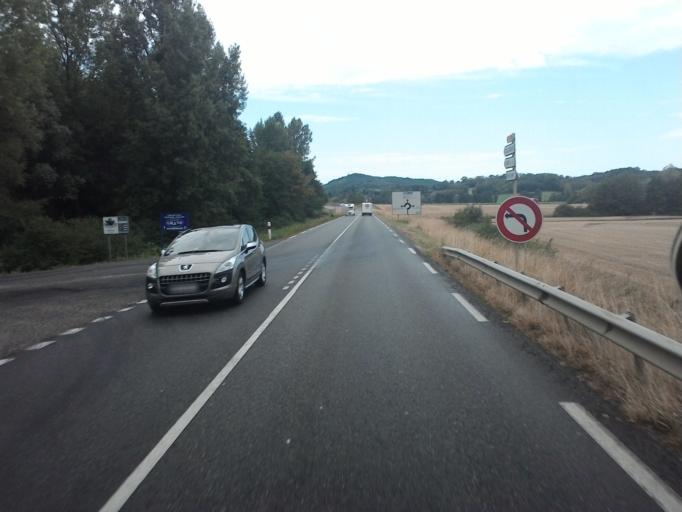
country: FR
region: Franche-Comte
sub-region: Departement du Jura
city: Poligny
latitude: 46.8143
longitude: 5.5891
